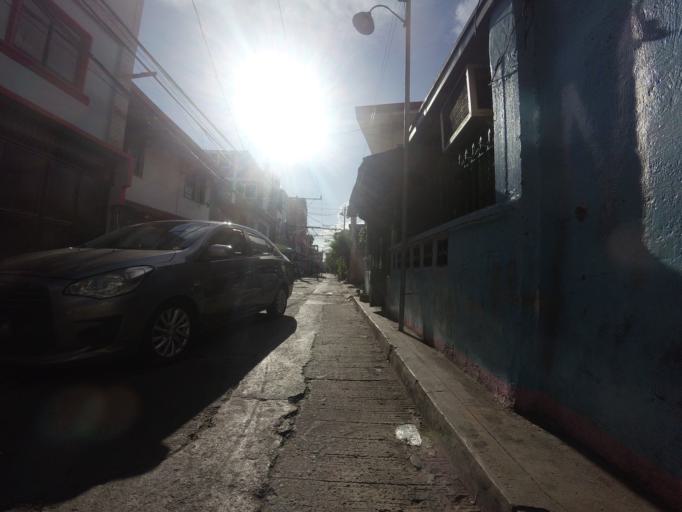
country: PH
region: Metro Manila
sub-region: Mandaluyong
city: Mandaluyong City
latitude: 14.5871
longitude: 121.0295
